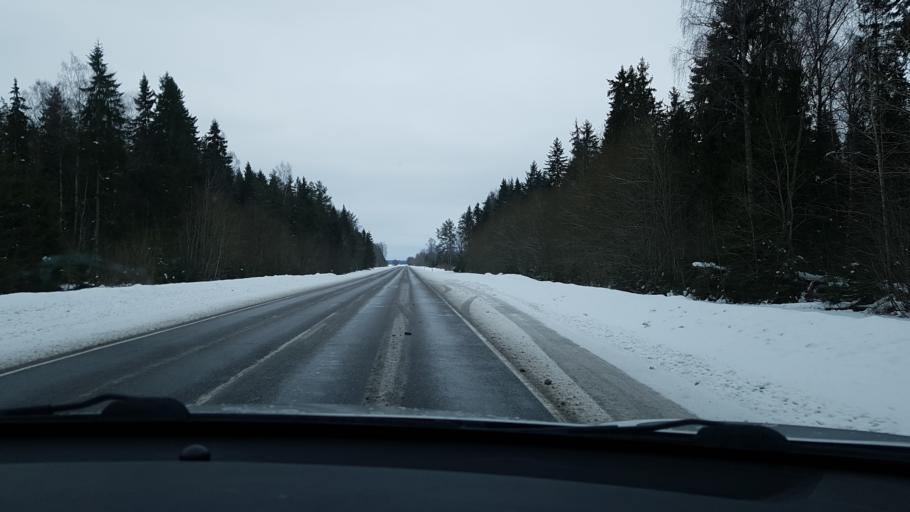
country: EE
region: Jaervamaa
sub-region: Jaerva-Jaani vald
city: Jarva-Jaani
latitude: 59.1328
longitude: 25.7768
